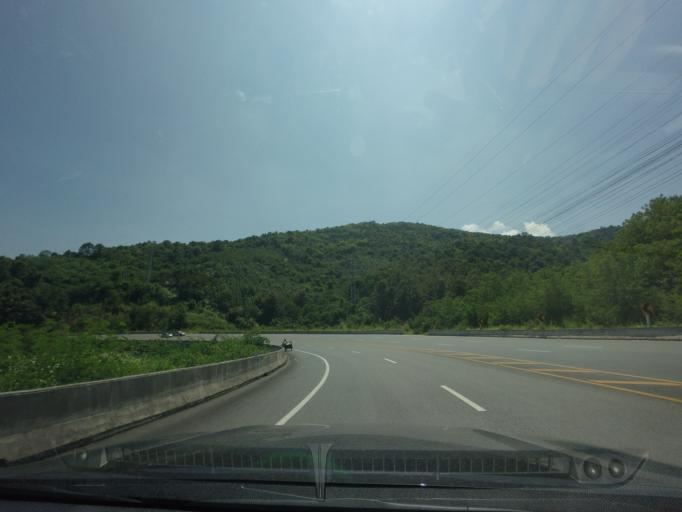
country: TH
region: Phetchabun
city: Lom Sak
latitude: 16.7724
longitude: 101.1218
